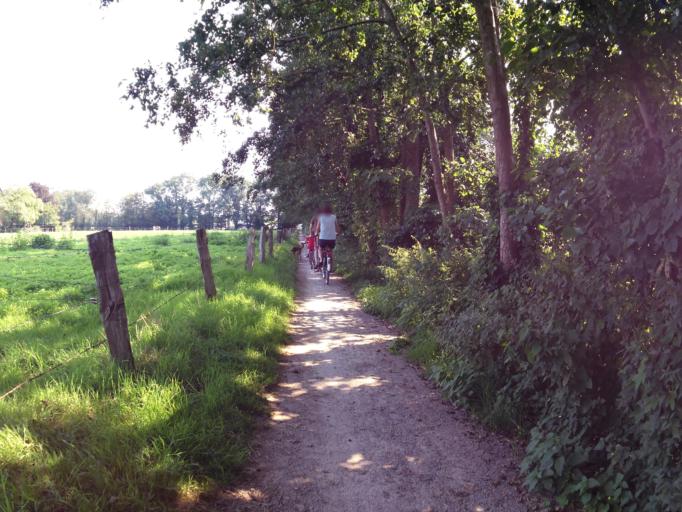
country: DE
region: North Rhine-Westphalia
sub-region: Regierungsbezirk Munster
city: Havixbeck
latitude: 51.9726
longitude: 7.4370
